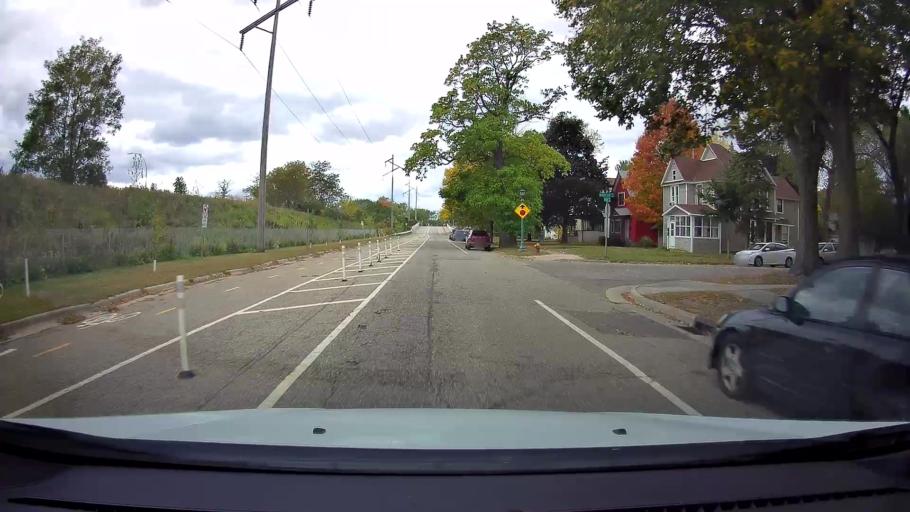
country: US
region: Minnesota
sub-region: Ramsey County
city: Falcon Heights
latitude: 44.9524
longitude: -93.1744
